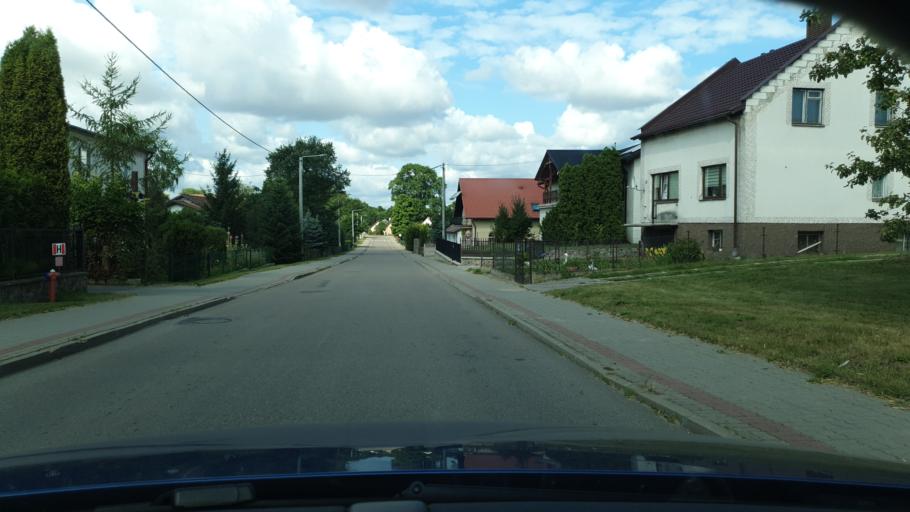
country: PL
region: Pomeranian Voivodeship
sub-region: Powiat czluchowski
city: Przechlewo
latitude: 53.8065
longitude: 17.3391
